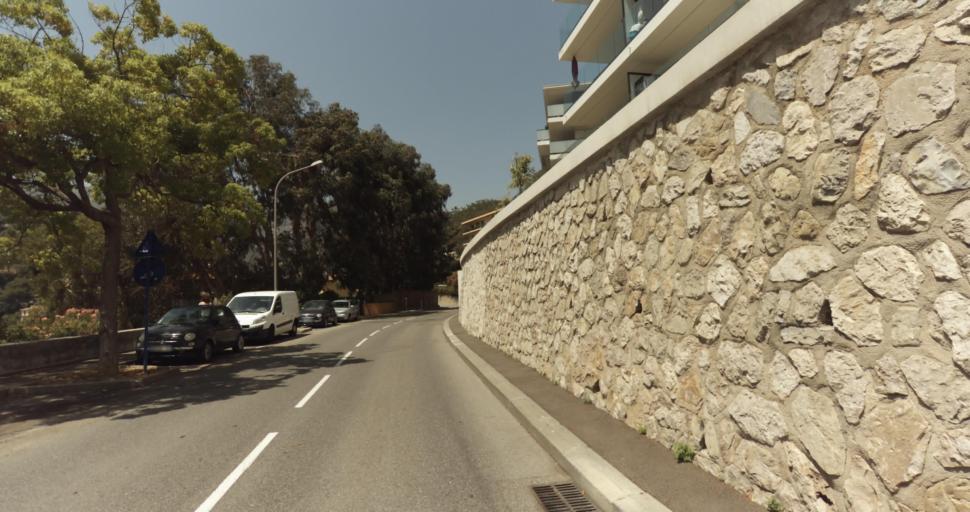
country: FR
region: Provence-Alpes-Cote d'Azur
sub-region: Departement des Alpes-Maritimes
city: Roquebrune-Cap-Martin
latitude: 43.7716
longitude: 7.4786
